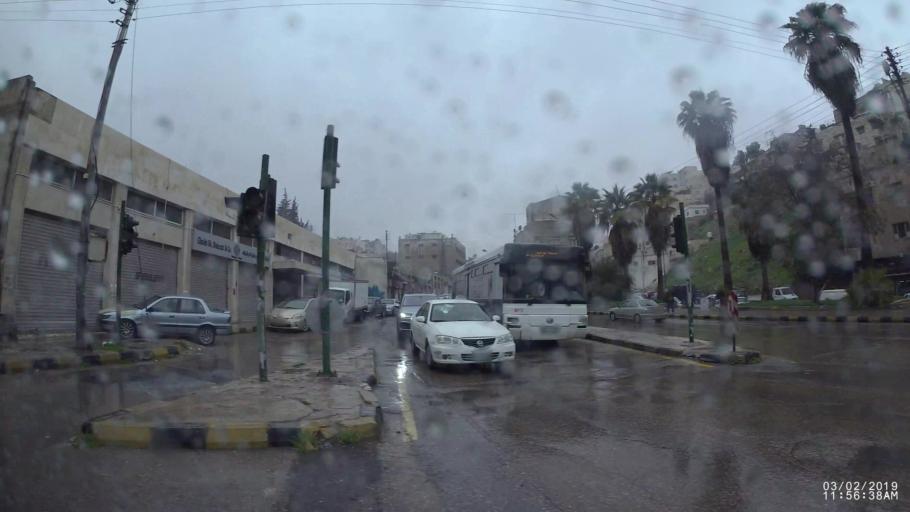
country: JO
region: Amman
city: Amman
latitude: 31.9588
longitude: 35.9257
